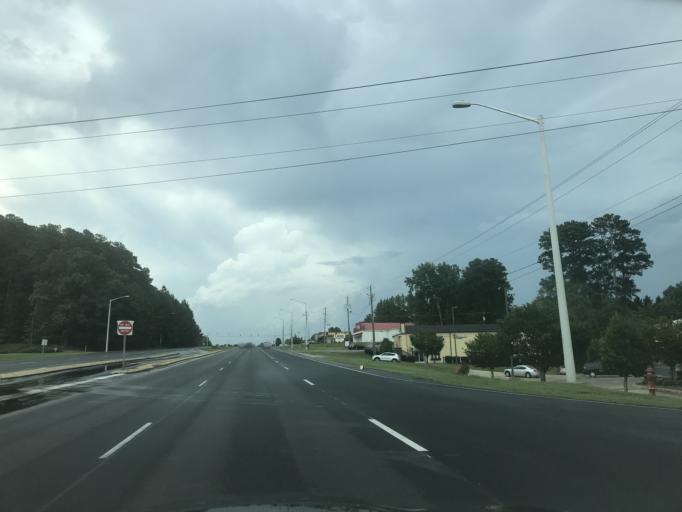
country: US
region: North Carolina
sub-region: Johnston County
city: Clayton
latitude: 35.6445
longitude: -78.4590
